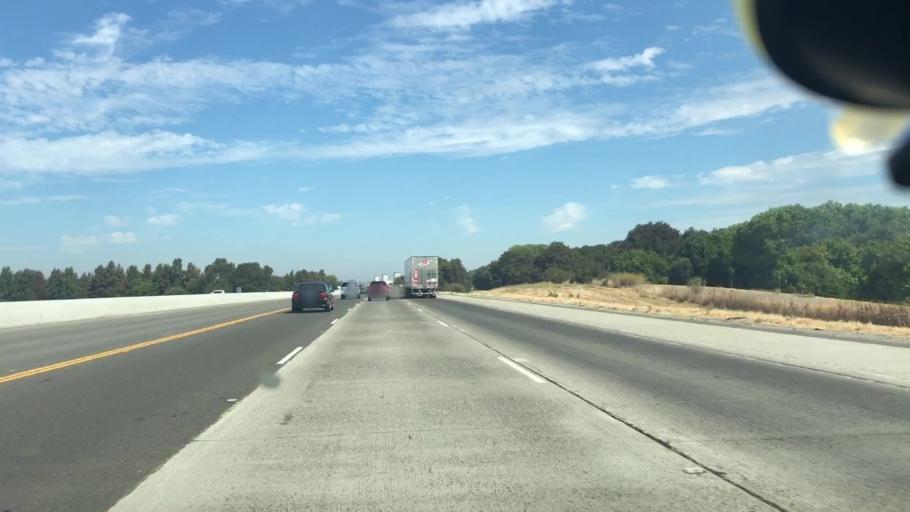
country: US
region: California
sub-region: Sacramento County
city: Parkway
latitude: 38.4474
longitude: -121.4915
